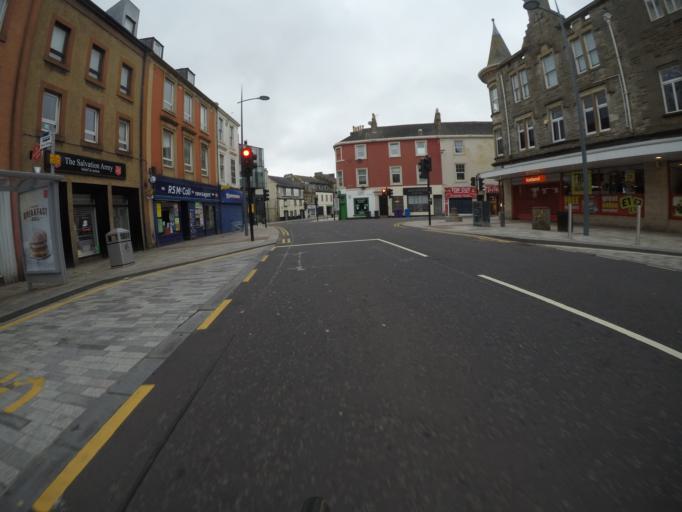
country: GB
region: Scotland
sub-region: North Ayrshire
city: Irvine
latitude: 55.6146
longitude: -4.6665
